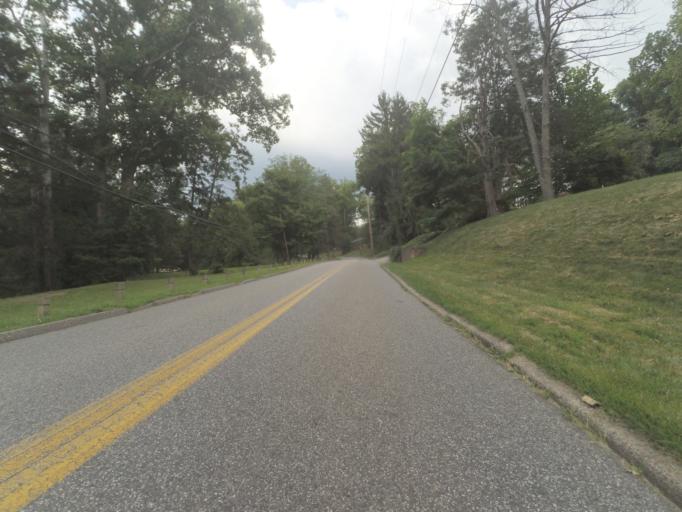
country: US
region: West Virginia
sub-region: Cabell County
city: Huntington
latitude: 38.4053
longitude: -82.4387
